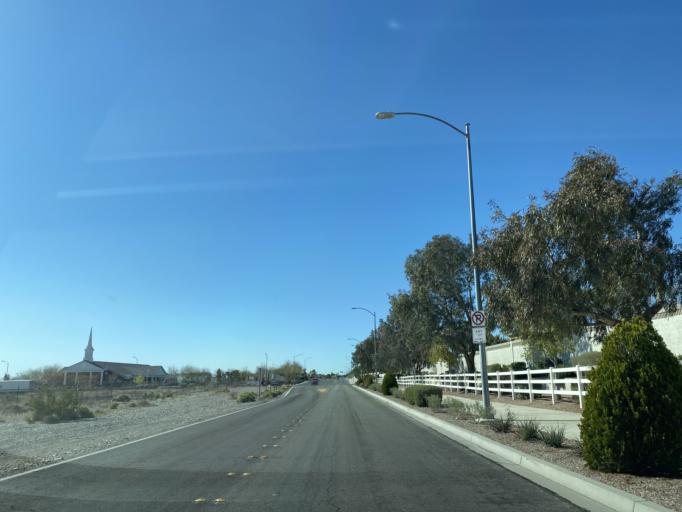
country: US
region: Nevada
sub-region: Clark County
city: Summerlin South
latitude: 36.3229
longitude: -115.2877
